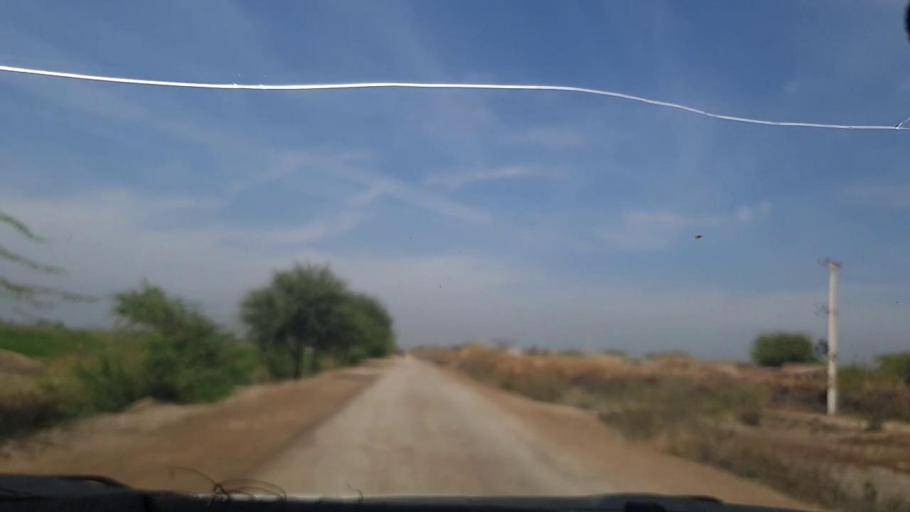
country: PK
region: Sindh
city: Pithoro
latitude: 25.4514
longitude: 69.4588
